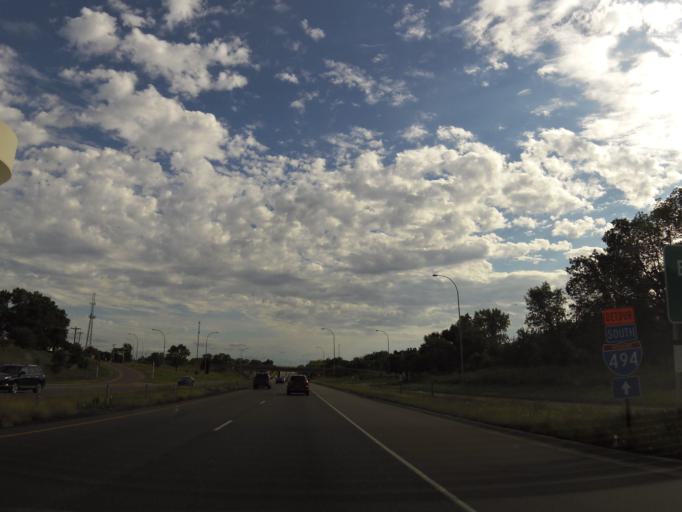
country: US
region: Minnesota
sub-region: Hennepin County
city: New Hope
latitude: 45.0102
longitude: -93.4011
